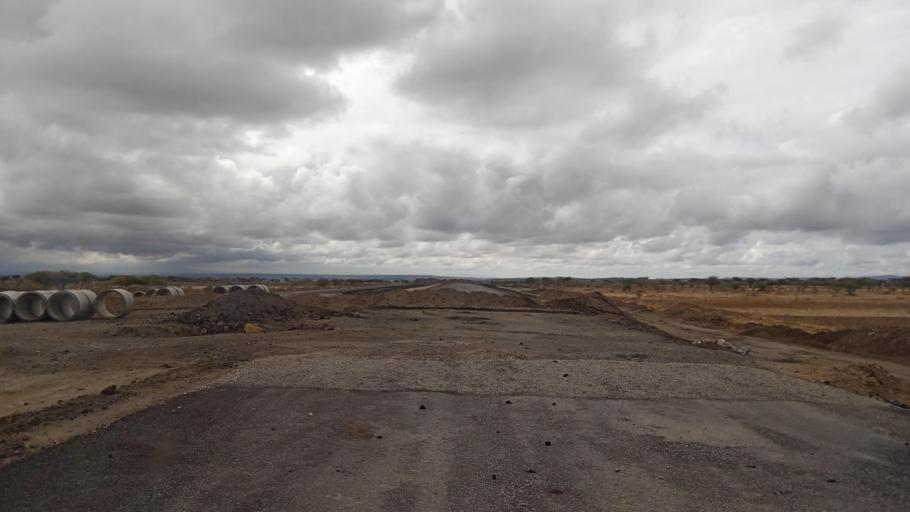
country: ET
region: Oromiya
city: Shashemene
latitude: 7.5573
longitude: 38.6736
